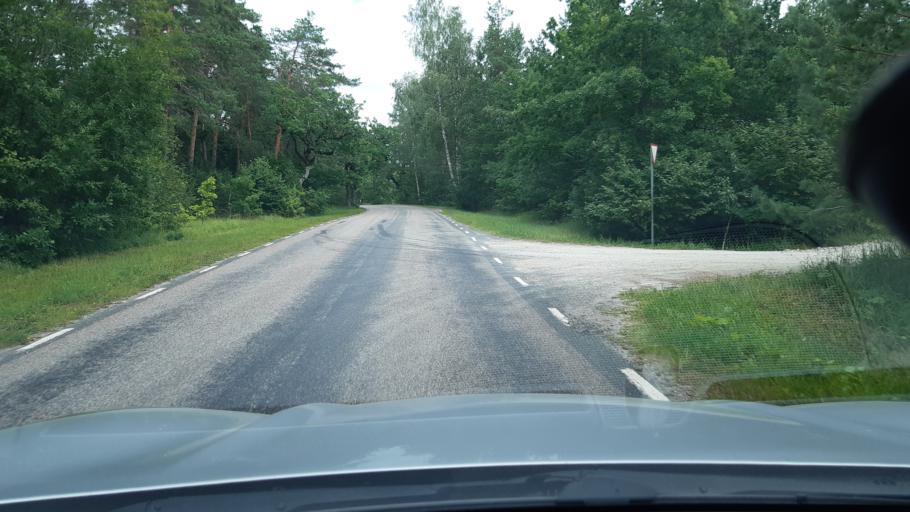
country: EE
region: Raplamaa
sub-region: Maerjamaa vald
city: Marjamaa
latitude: 59.0402
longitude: 24.5066
